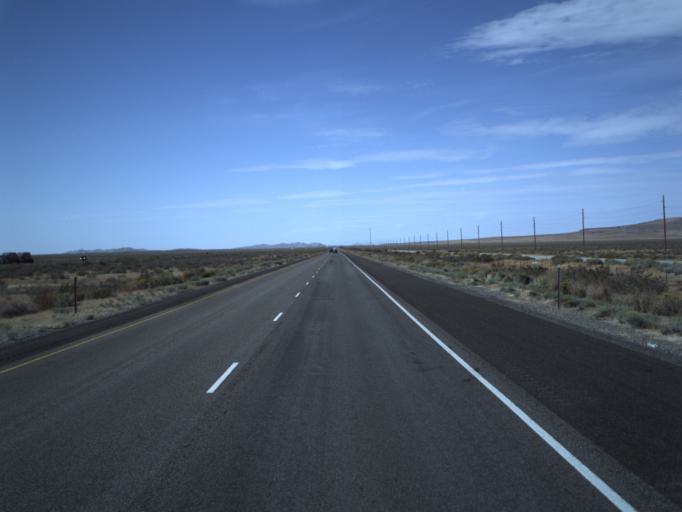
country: US
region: Utah
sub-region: Tooele County
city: Grantsville
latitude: 40.7471
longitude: -113.0604
